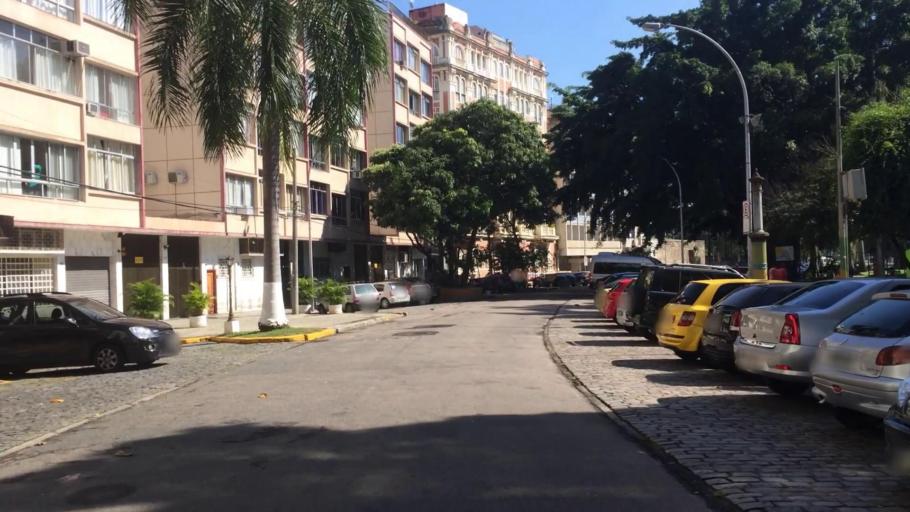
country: BR
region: Rio de Janeiro
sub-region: Rio De Janeiro
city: Rio de Janeiro
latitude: -22.9222
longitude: -43.1742
